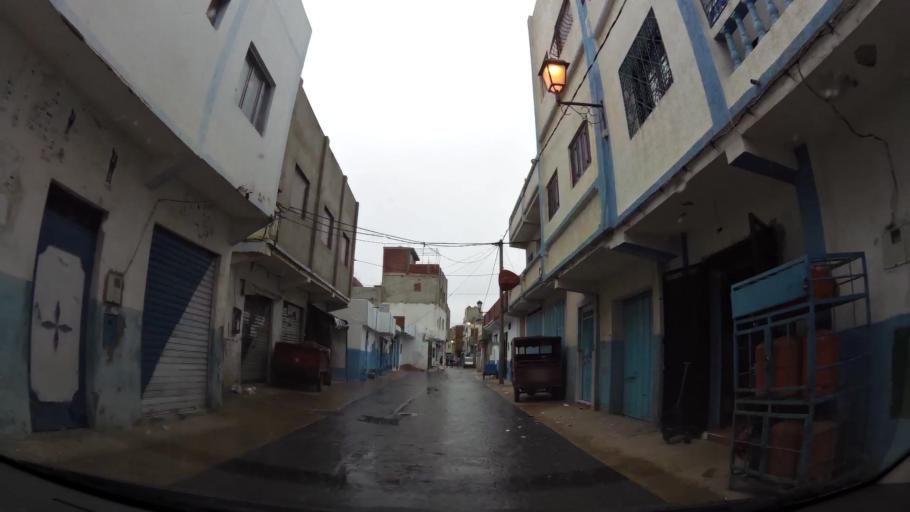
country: MA
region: Tanger-Tetouan
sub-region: Tetouan
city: Martil
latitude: 35.6215
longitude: -5.2808
